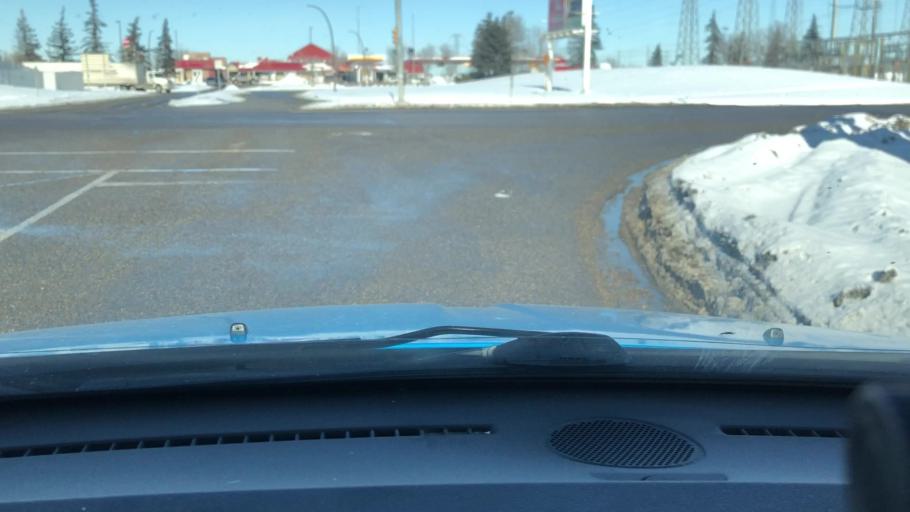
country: CA
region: Alberta
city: Calgary
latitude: 51.0084
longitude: -114.0041
